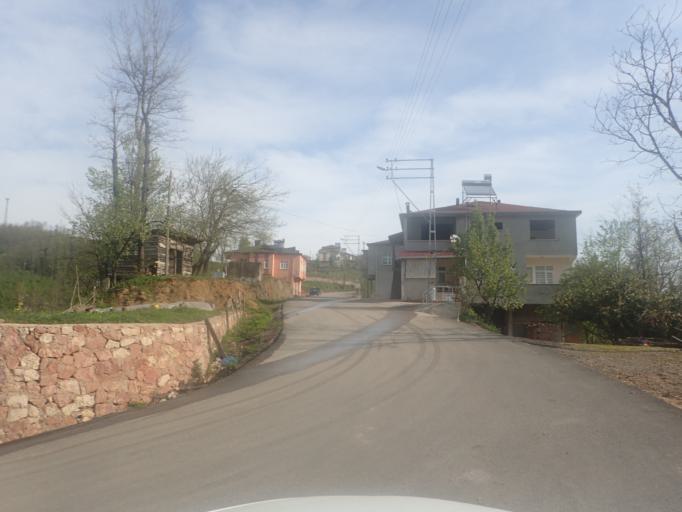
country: TR
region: Ordu
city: Catalpinar
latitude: 40.8828
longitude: 37.4892
